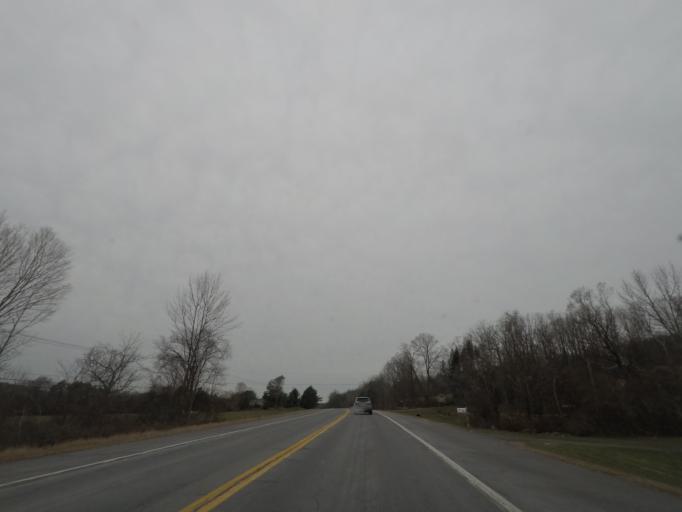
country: US
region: Massachusetts
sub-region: Berkshire County
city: Lanesborough
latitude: 42.5417
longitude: -73.3468
